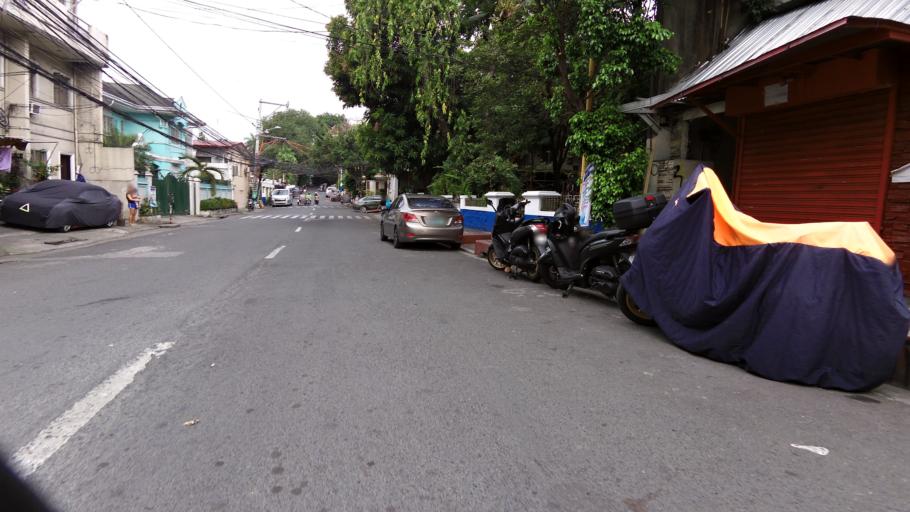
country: PH
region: Metro Manila
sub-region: Pasig
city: Pasig City
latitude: 14.5659
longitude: 121.0594
